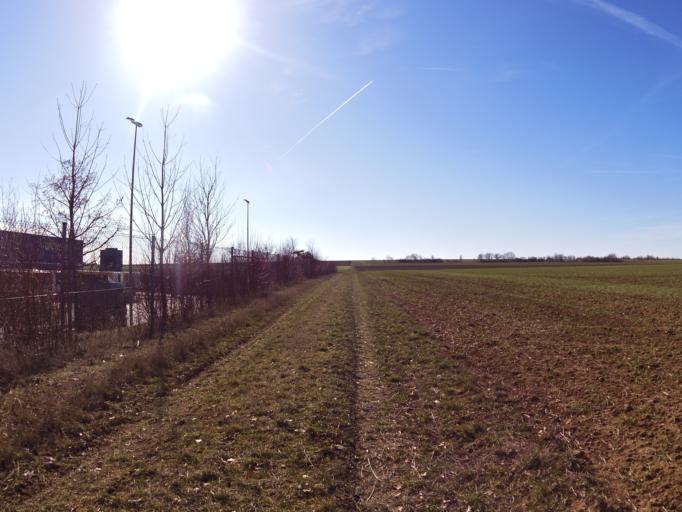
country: DE
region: Bavaria
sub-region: Regierungsbezirk Unterfranken
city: Kurnach
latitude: 49.8510
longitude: 10.0247
